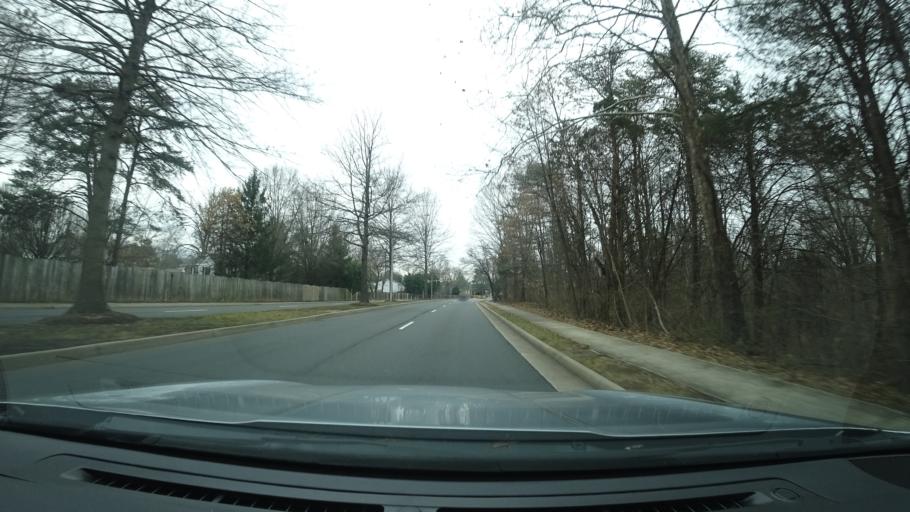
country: US
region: Virginia
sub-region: Fairfax County
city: Herndon
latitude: 38.9757
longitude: -77.3711
